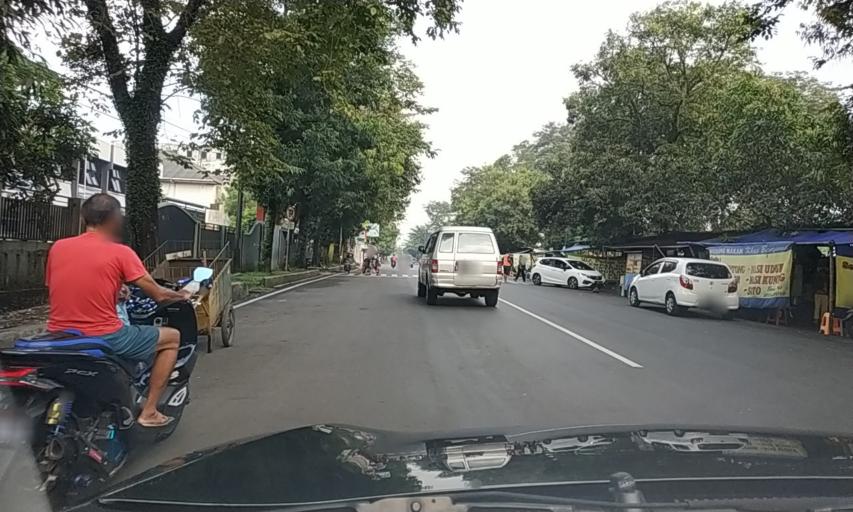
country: ID
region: Central Java
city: Purwokerto
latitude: -7.4174
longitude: 109.2506
